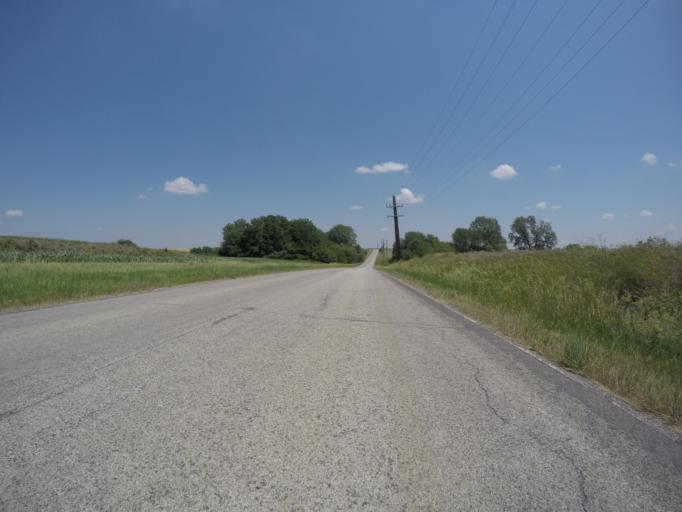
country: US
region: Kansas
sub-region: Doniphan County
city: Troy
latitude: 39.7672
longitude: -95.1259
